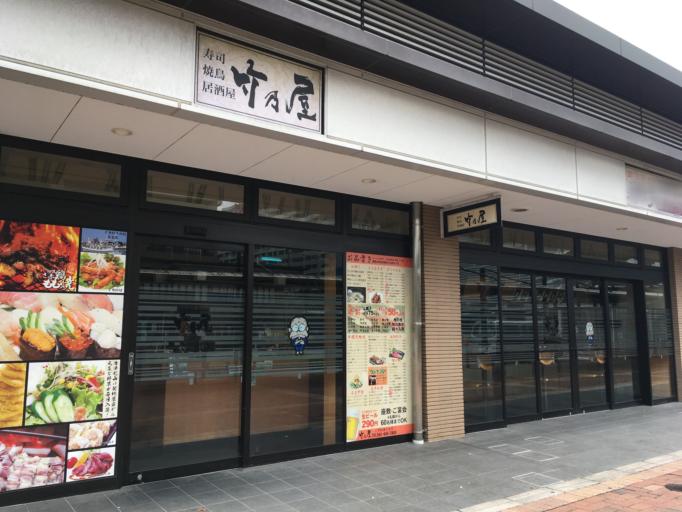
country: JP
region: Fukuoka
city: Fukuoka-shi
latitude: 33.6066
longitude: 130.4229
